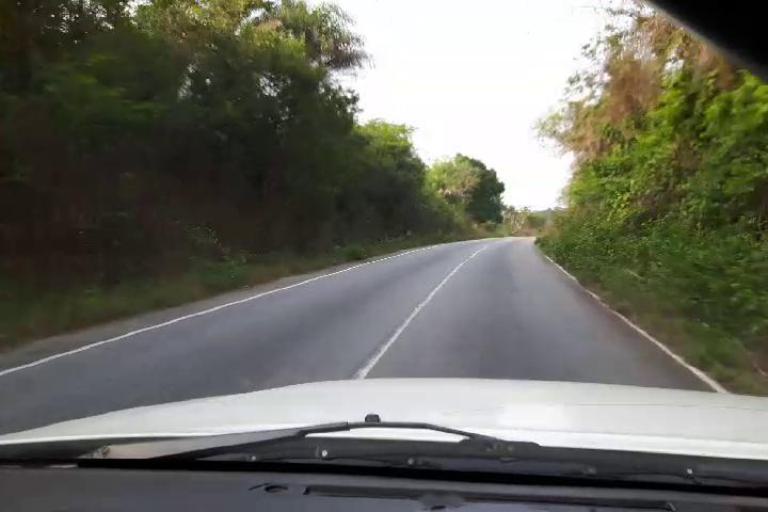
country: SL
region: Southern Province
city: Palima
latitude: 7.9317
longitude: -11.5288
